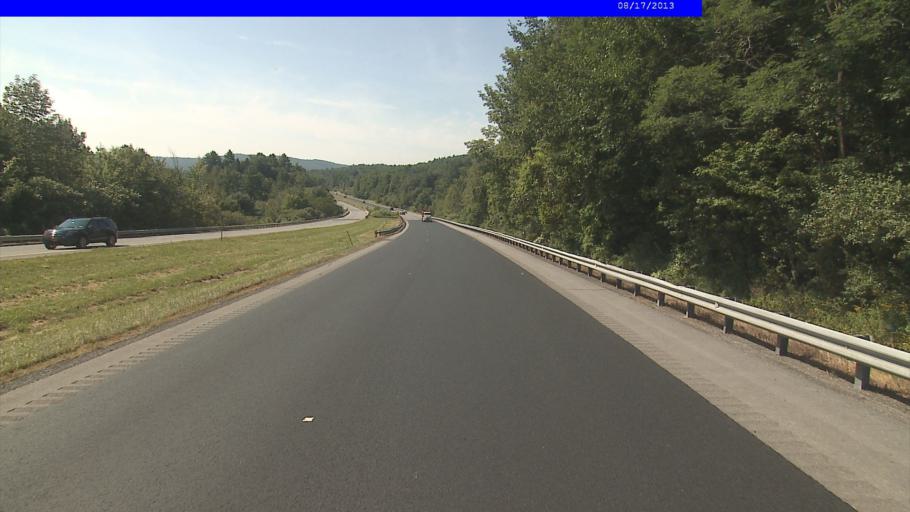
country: US
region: New Hampshire
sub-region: Cheshire County
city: Westmoreland
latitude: 42.9928
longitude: -72.4766
